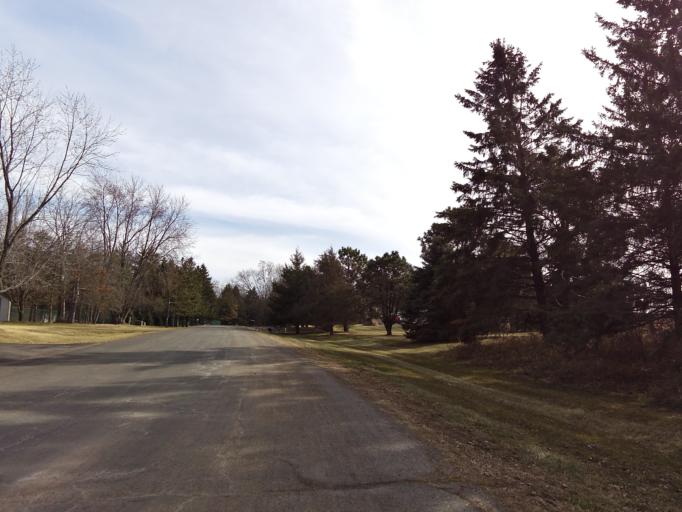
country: US
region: Minnesota
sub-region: Washington County
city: Lakeland
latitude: 44.9451
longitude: -92.7839
